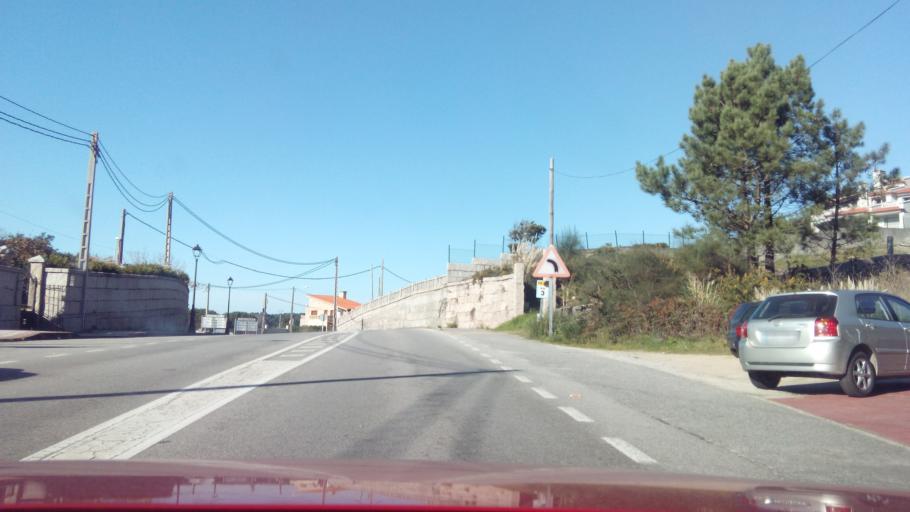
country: ES
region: Galicia
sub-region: Provincia de Pontevedra
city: O Grove
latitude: 42.4648
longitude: -8.9044
